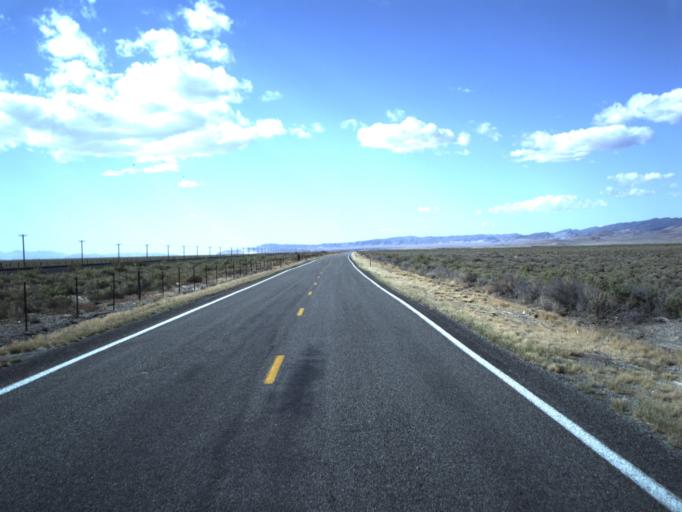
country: US
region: Utah
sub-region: Millard County
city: Delta
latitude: 39.1362
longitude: -112.7279
